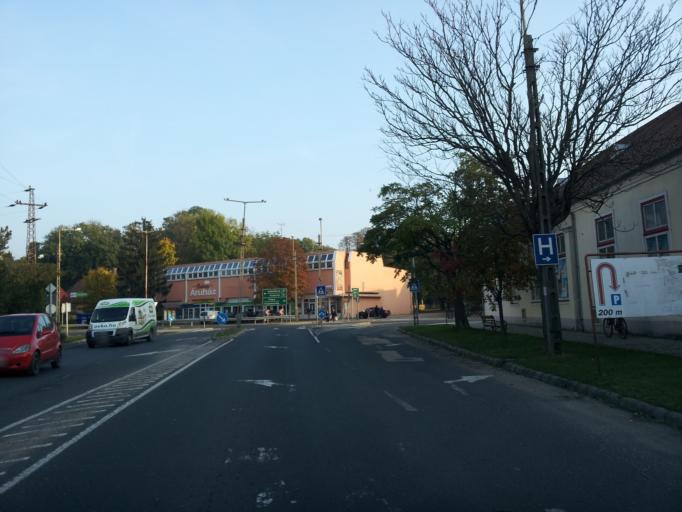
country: HU
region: Komarom-Esztergom
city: Kisber
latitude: 47.5022
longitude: 18.0265
